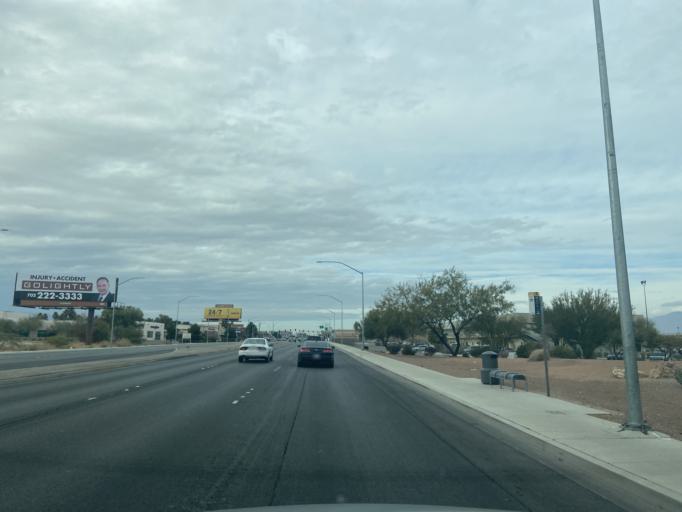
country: US
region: Nevada
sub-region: Clark County
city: Las Vegas
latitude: 36.2072
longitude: -115.2028
